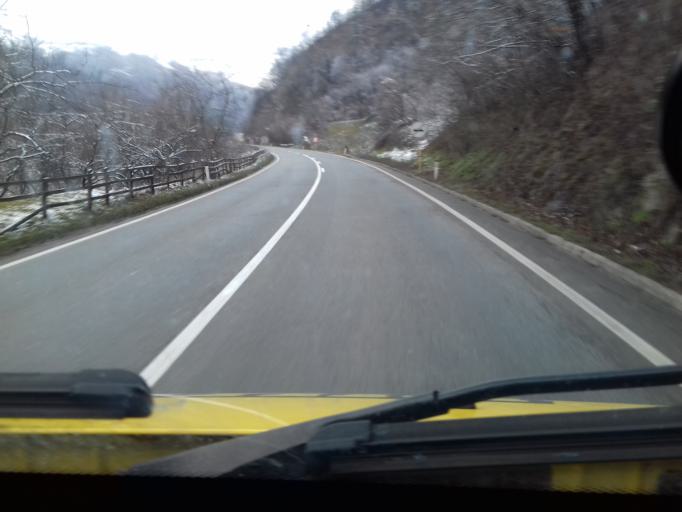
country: BA
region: Federation of Bosnia and Herzegovina
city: Zeljezno Polje
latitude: 44.3368
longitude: 17.9228
